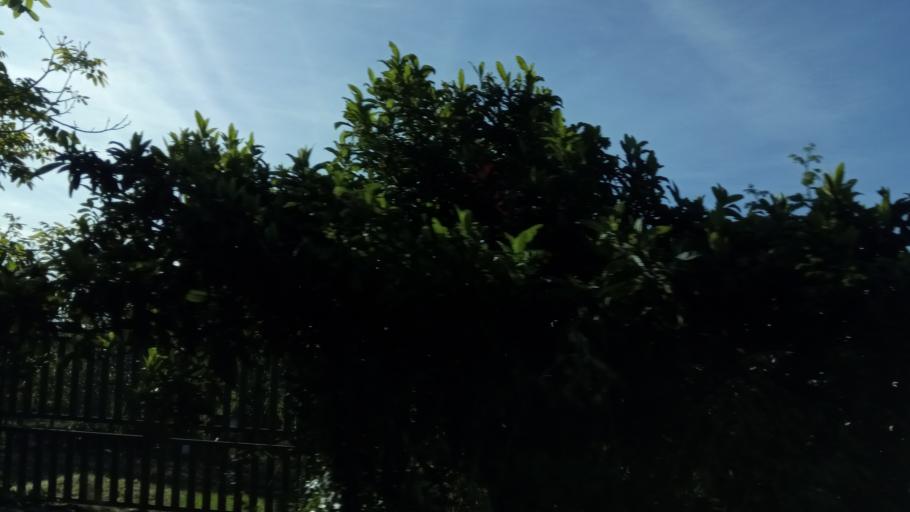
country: IT
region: Latium
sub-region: Provincia di Latina
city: Grunuovo-Campomaggiore San Luca
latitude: 41.2666
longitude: 13.7837
